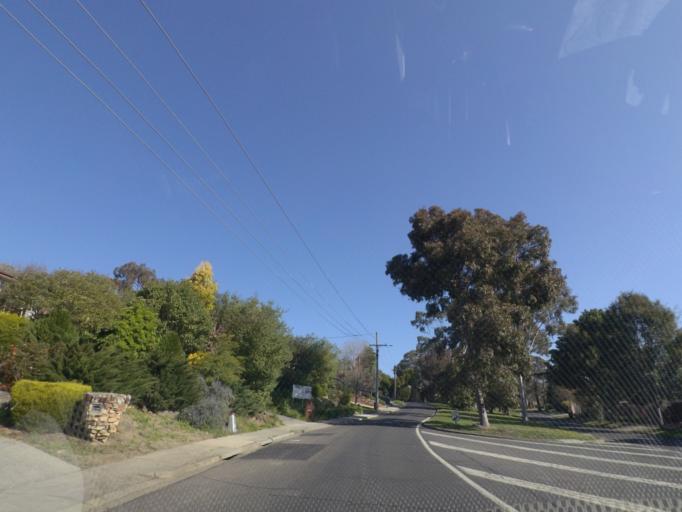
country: AU
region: Victoria
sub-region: Whitehorse
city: Mont Albert North
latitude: -37.7967
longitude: 145.1039
